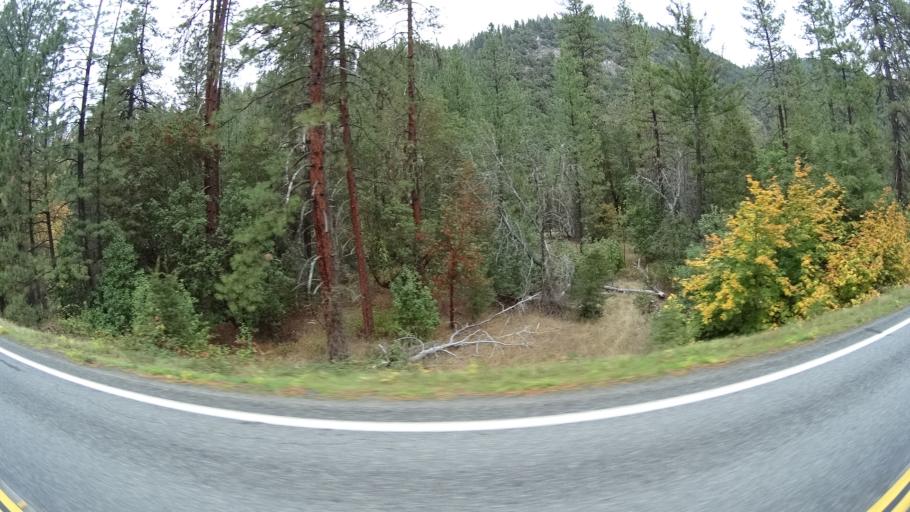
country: US
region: California
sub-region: Siskiyou County
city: Happy Camp
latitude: 41.8344
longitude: -123.1799
